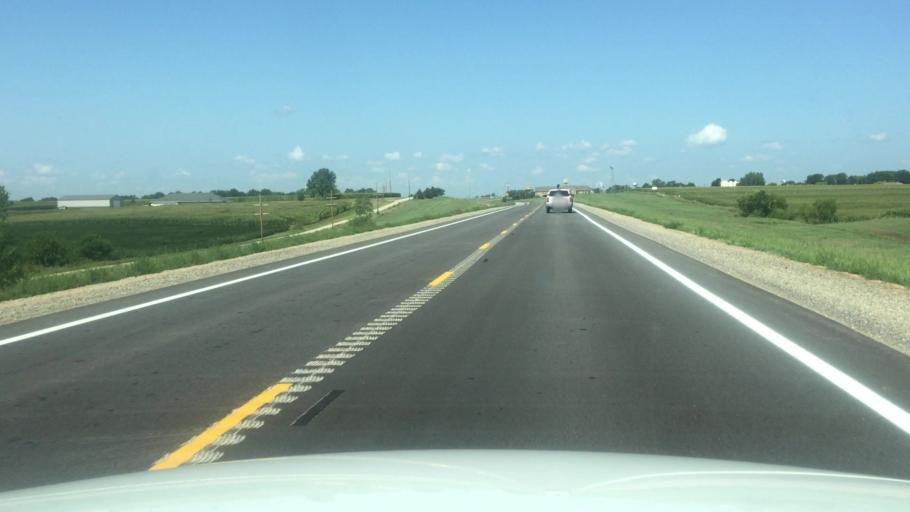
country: US
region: Kansas
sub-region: Brown County
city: Hiawatha
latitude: 39.8421
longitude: -95.5148
